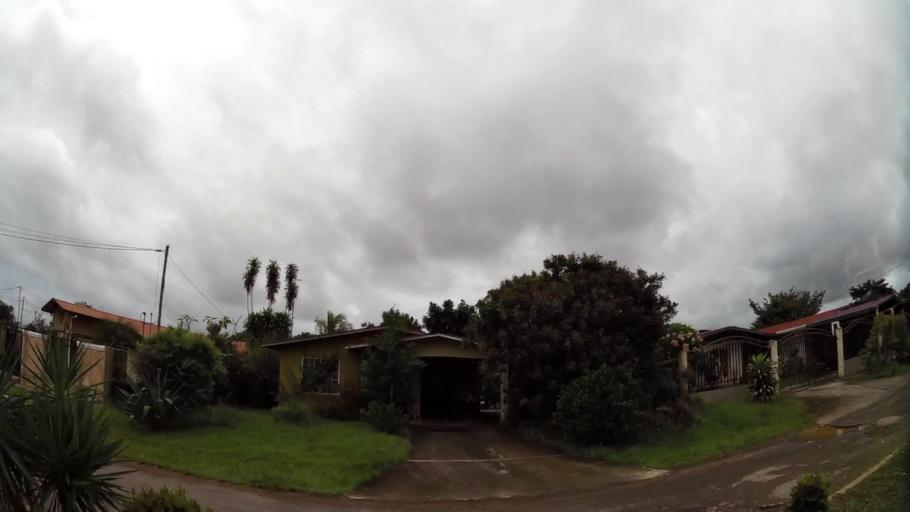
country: PA
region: Chiriqui
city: David
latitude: 8.4165
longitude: -82.4539
